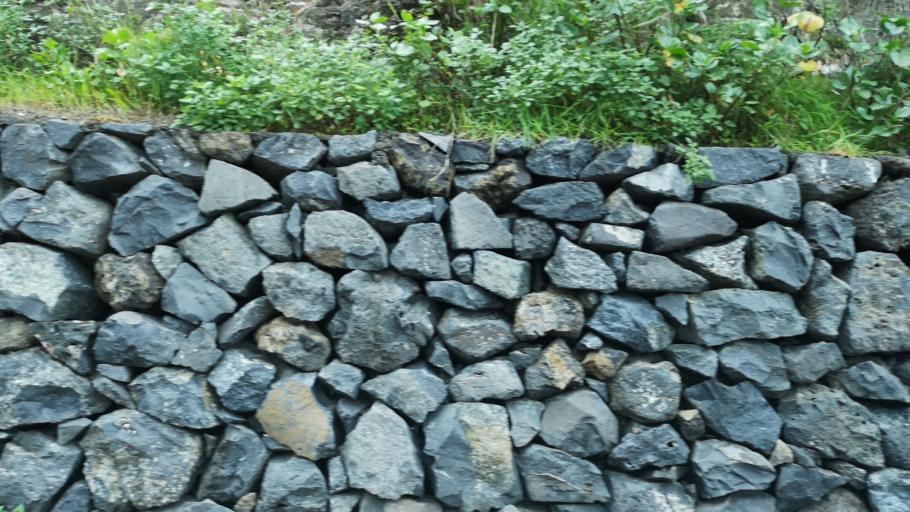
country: ES
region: Canary Islands
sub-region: Provincia de Santa Cruz de Tenerife
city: Hermigua
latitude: 28.1364
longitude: -17.1974
